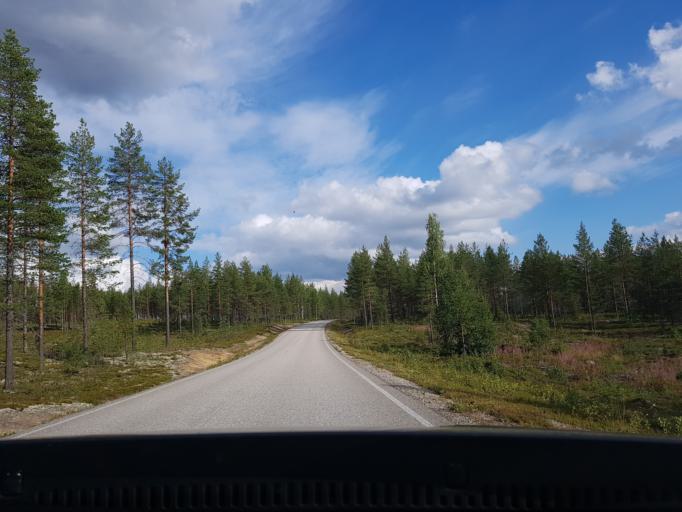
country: FI
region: Kainuu
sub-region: Kehys-Kainuu
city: Kuhmo
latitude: 64.6198
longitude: 29.7054
